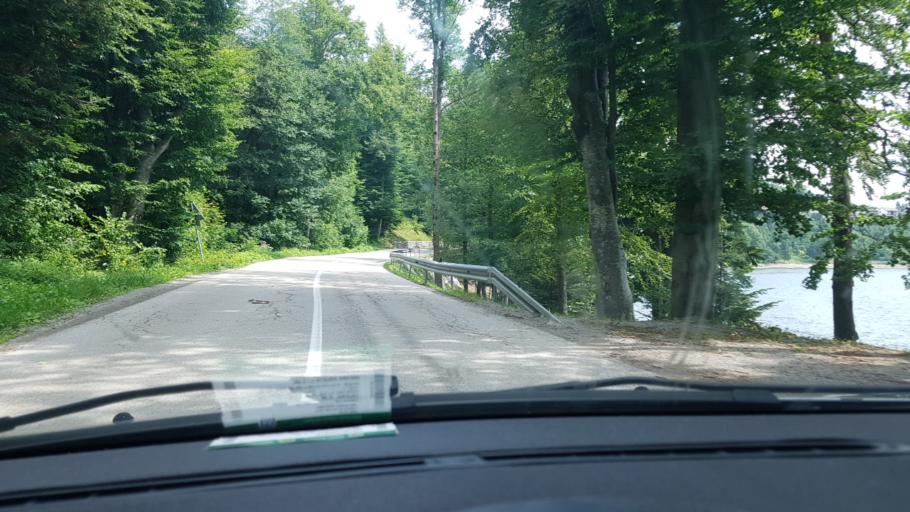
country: HR
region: Primorsko-Goranska
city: Hreljin
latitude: 45.3158
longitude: 14.7136
